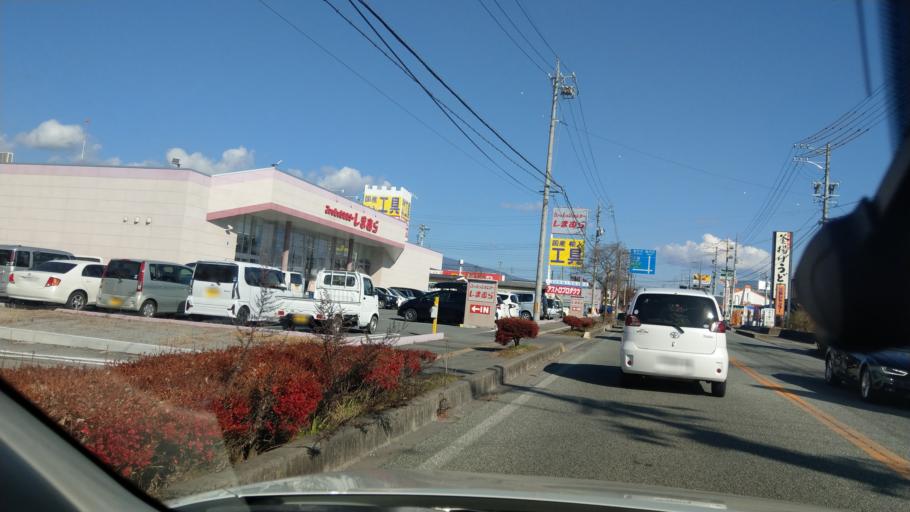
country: JP
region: Nagano
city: Komoro
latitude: 36.2822
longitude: 138.4815
